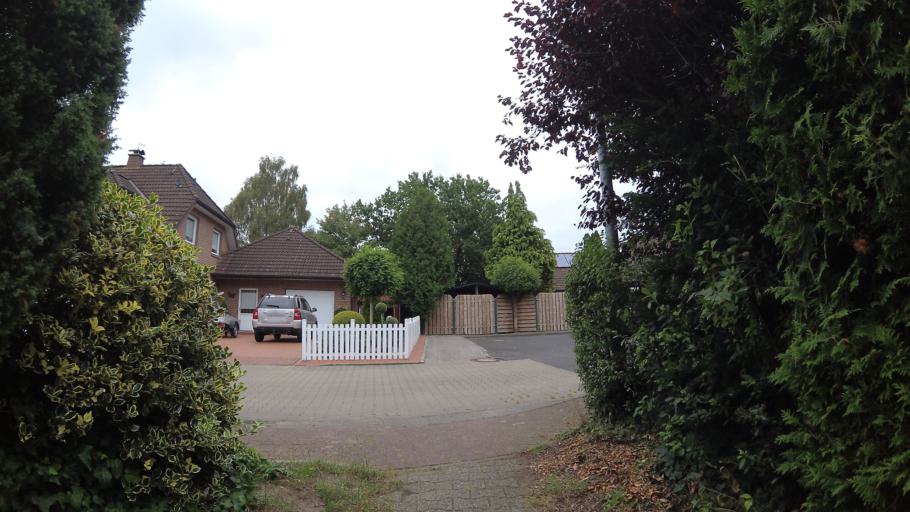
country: DE
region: Lower Saxony
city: Fresenburg
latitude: 52.8828
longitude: 7.3065
